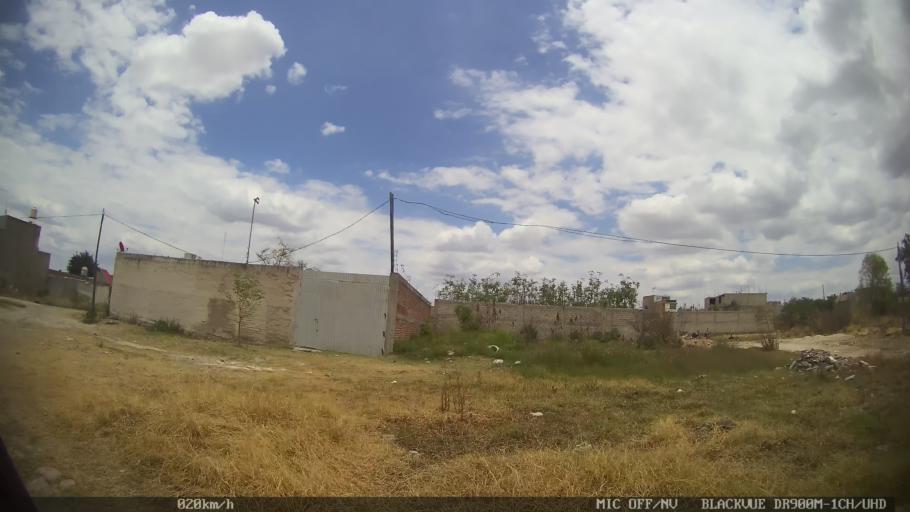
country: MX
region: Jalisco
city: Tlaquepaque
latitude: 20.6411
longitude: -103.2701
